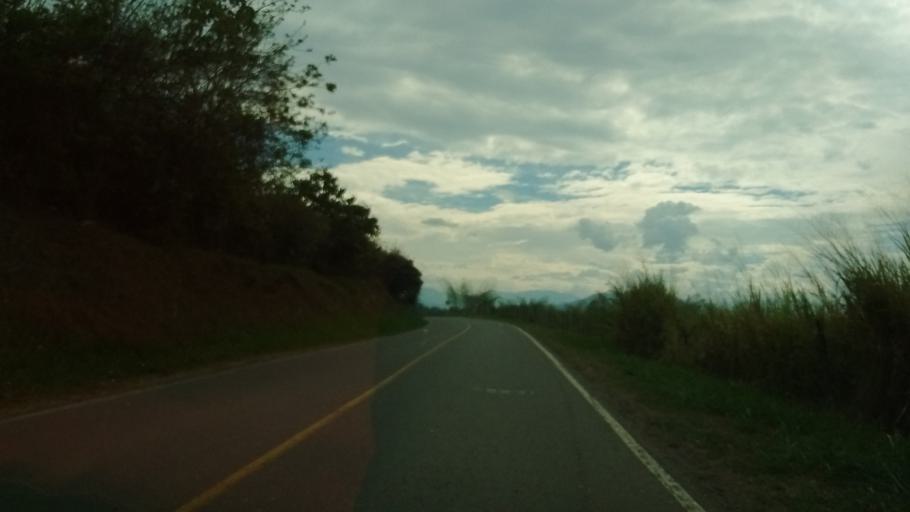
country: CO
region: Cauca
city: Santander de Quilichao
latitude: 3.0352
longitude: -76.4691
